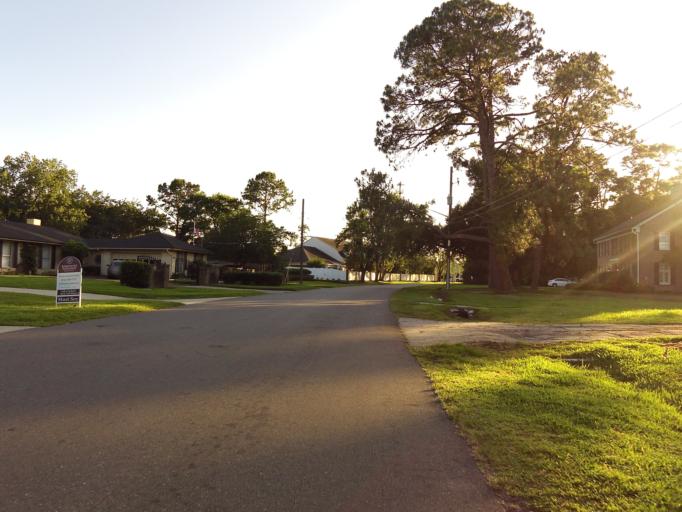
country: US
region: Florida
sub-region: Clay County
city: Orange Park
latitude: 30.2526
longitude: -81.6963
